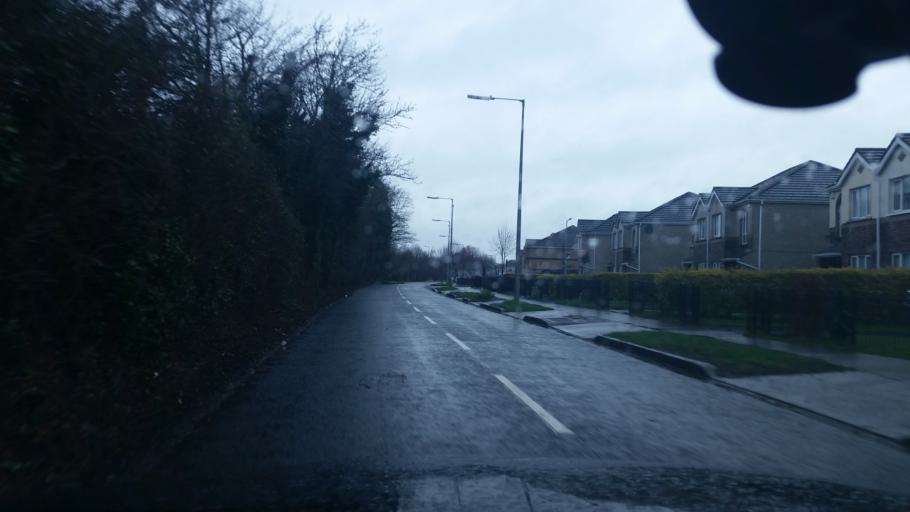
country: IE
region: Leinster
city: Hartstown
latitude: 53.3849
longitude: -6.4097
